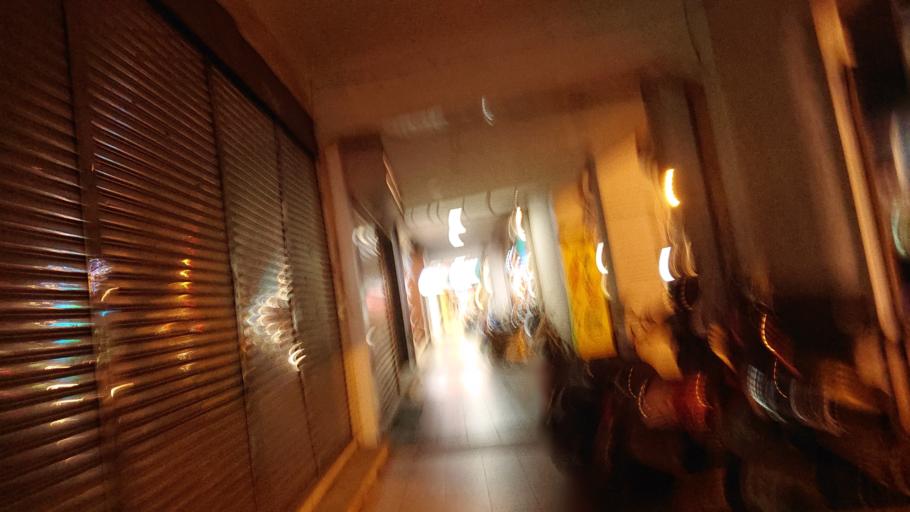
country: TW
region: Taiwan
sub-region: Tainan
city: Tainan
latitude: 22.9940
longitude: 120.2009
